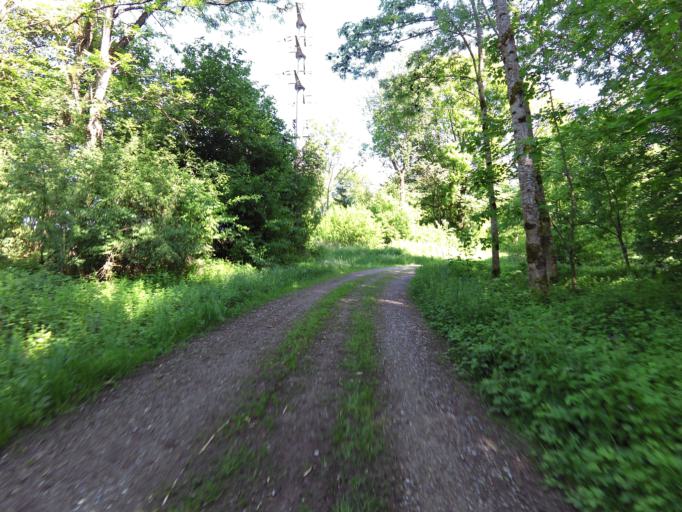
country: CH
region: Thurgau
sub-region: Frauenfeld District
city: Mullheim
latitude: 47.5870
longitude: 9.0045
